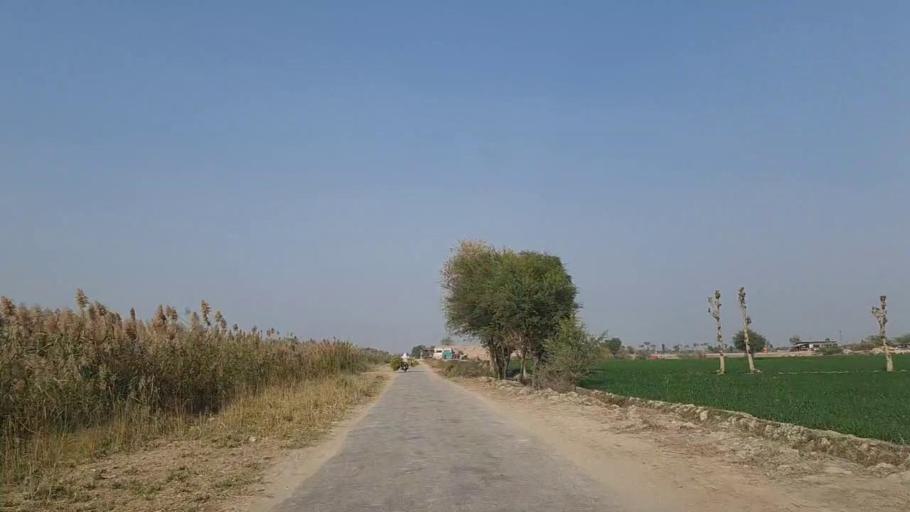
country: PK
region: Sindh
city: Daur
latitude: 26.4731
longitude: 68.4661
